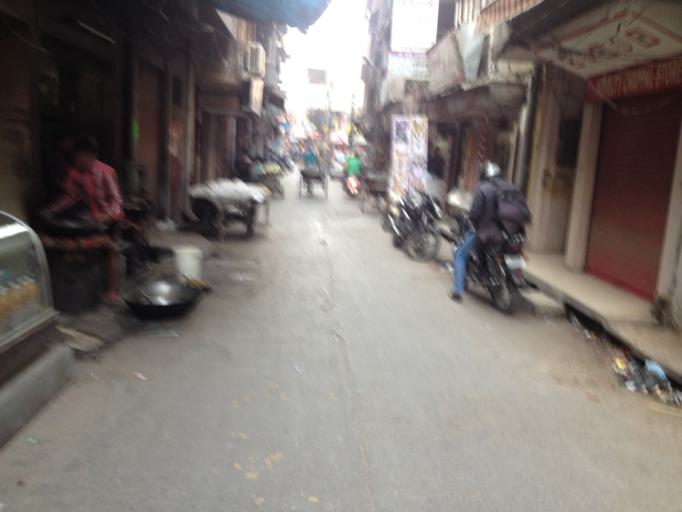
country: IN
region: Punjab
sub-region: Amritsar
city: Amritsar
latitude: 31.6180
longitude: 74.8749
